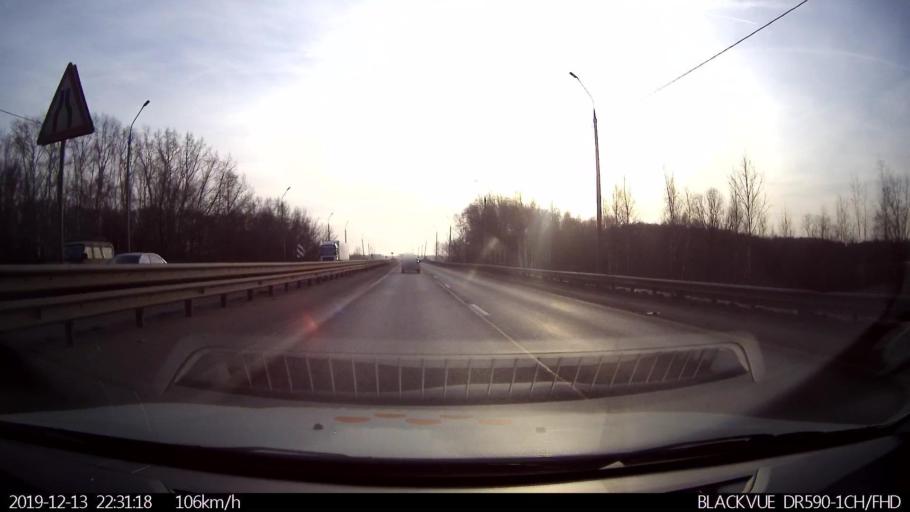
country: RU
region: Nizjnij Novgorod
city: Afonino
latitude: 56.2200
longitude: 44.0774
